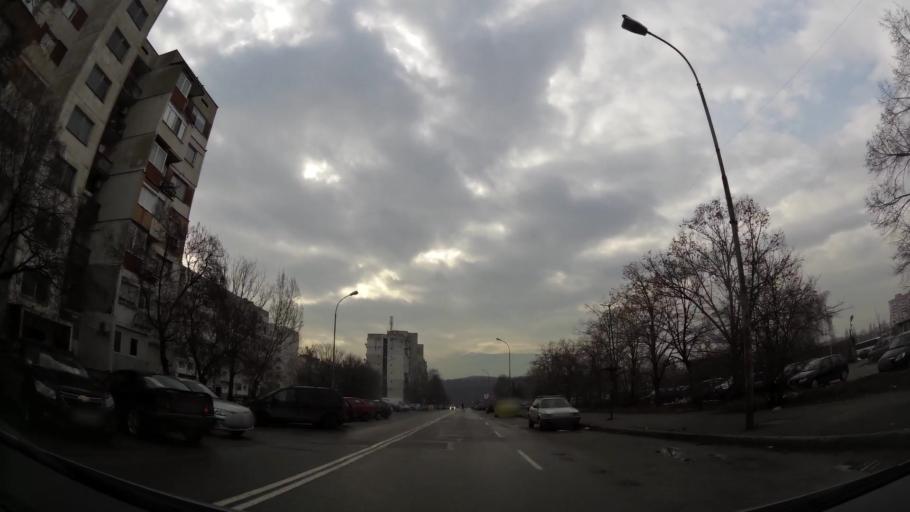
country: BG
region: Sofia-Capital
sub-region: Stolichna Obshtina
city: Sofia
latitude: 42.7130
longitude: 23.2585
